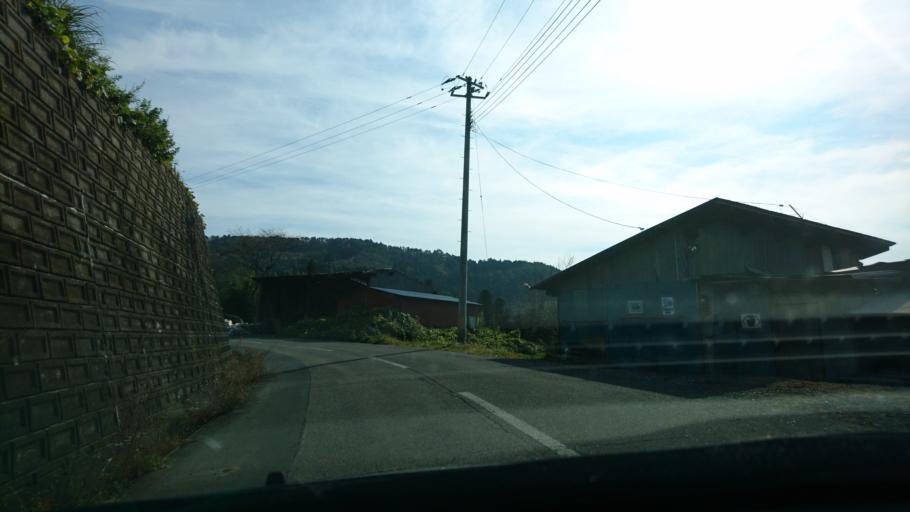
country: JP
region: Iwate
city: Ichinoseki
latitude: 38.9764
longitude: 141.1784
